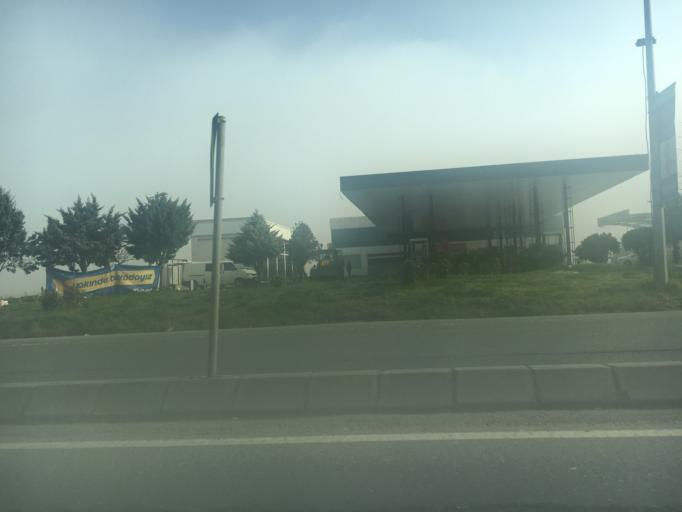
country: TR
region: Istanbul
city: Esenyurt
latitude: 41.0508
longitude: 28.6872
